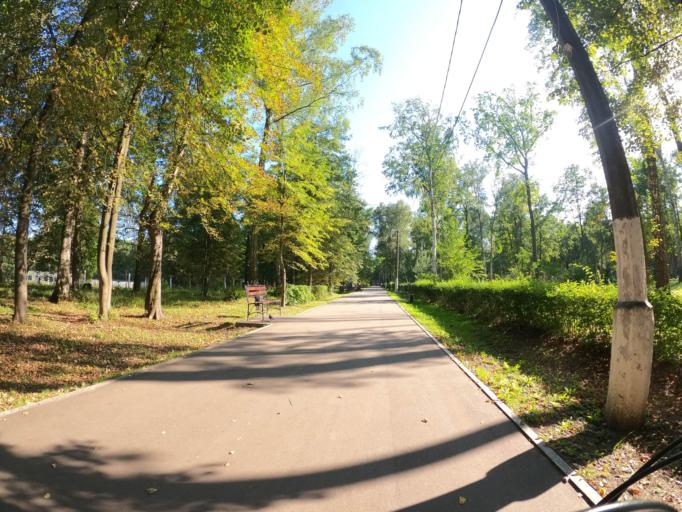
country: RU
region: Moskovskaya
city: Stupino
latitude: 54.8826
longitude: 38.0863
